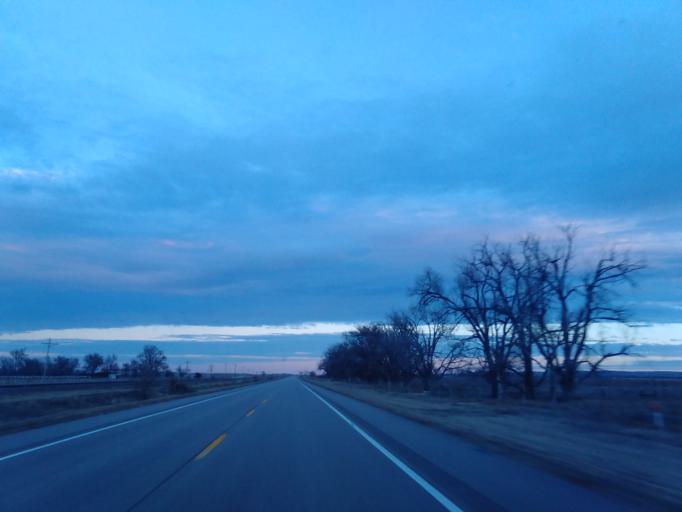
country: US
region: Nebraska
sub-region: Garden County
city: Oshkosh
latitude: 41.3936
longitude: -102.3080
